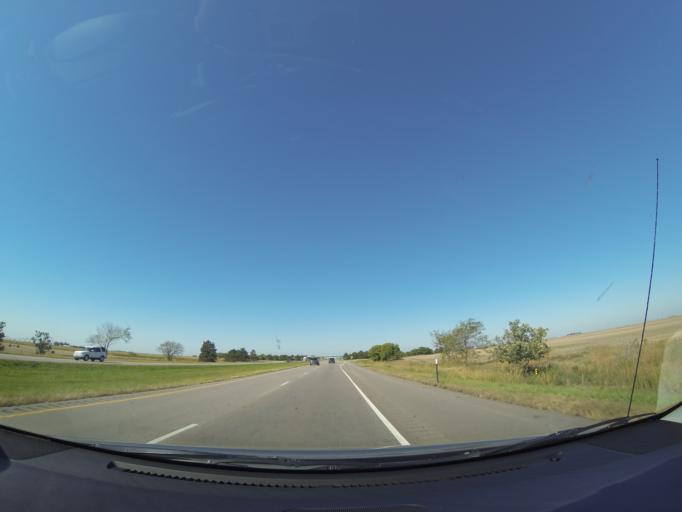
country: US
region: Nebraska
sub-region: Saline County
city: Friend
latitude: 40.8223
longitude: -97.2845
